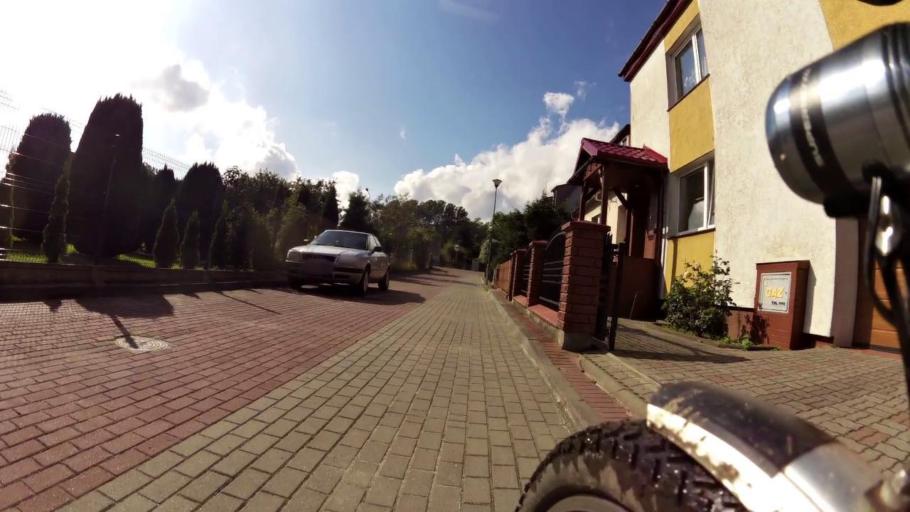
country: PL
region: West Pomeranian Voivodeship
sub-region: Powiat swidwinski
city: Swidwin
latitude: 53.7662
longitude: 15.7603
